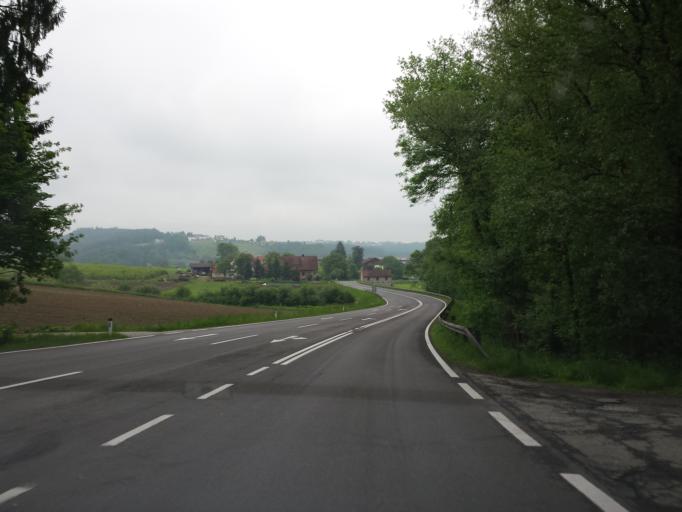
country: AT
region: Styria
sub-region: Politischer Bezirk Weiz
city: Mitterdorf an der Raab
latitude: 47.1680
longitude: 15.6094
